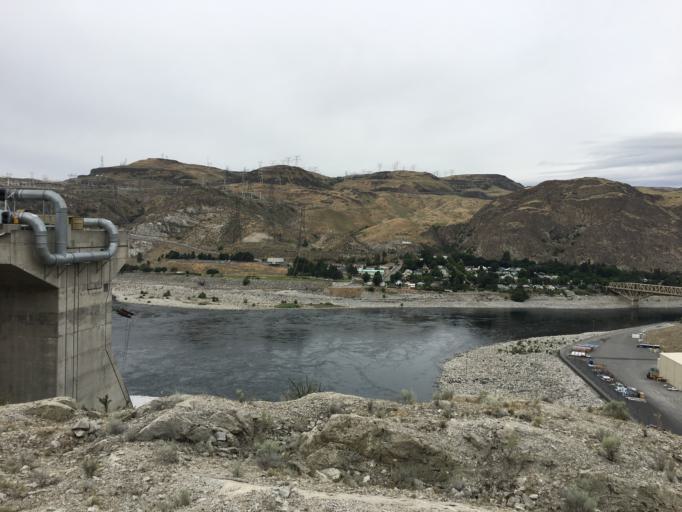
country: US
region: Washington
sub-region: Okanogan County
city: Coulee Dam
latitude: 47.9607
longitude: -118.9722
